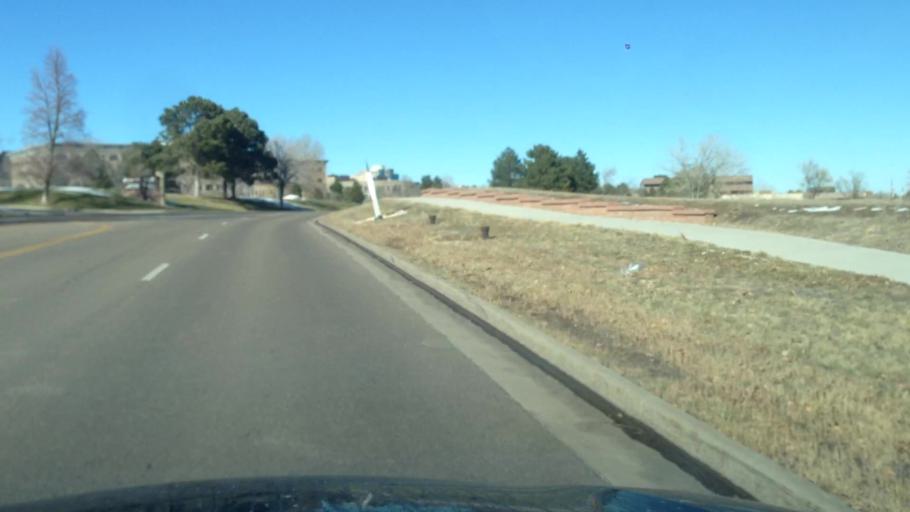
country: US
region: Colorado
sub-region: Douglas County
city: Meridian
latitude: 39.5600
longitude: -104.8653
